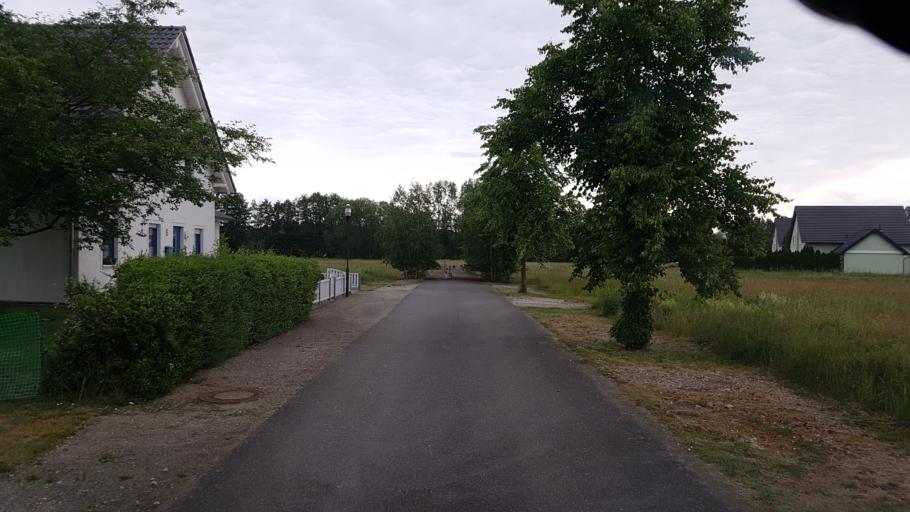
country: DE
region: Saxony-Anhalt
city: Holzdorf
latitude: 51.8172
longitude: 13.2249
